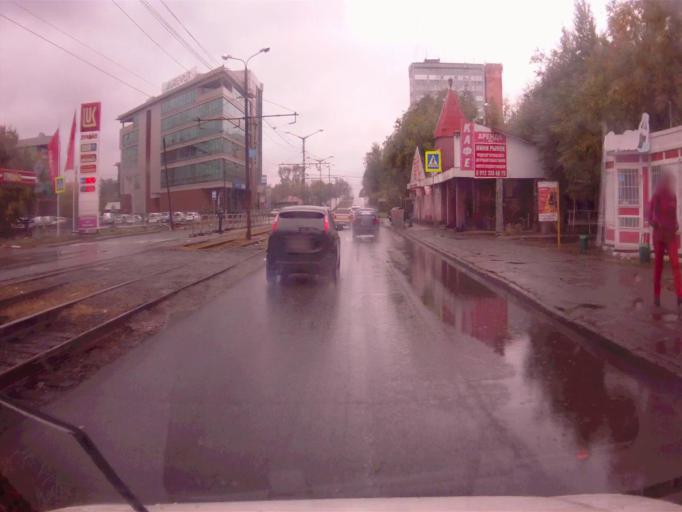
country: RU
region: Chelyabinsk
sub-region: Gorod Chelyabinsk
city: Chelyabinsk
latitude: 55.1691
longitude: 61.4157
